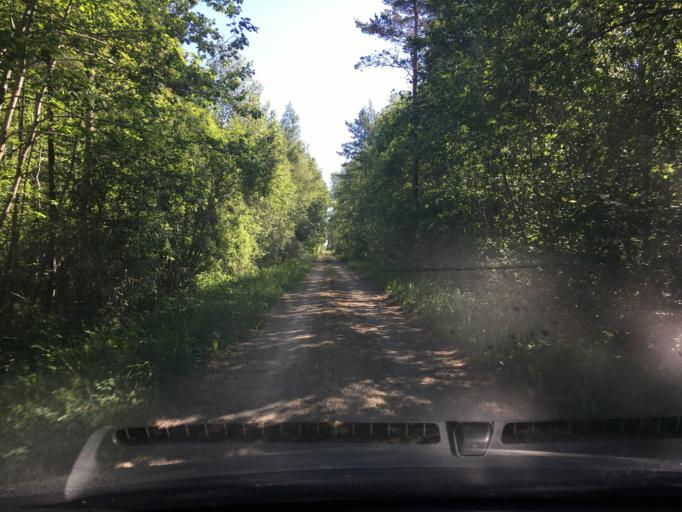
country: EE
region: Laeaene
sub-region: Lihula vald
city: Lihula
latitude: 58.6209
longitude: 23.7038
